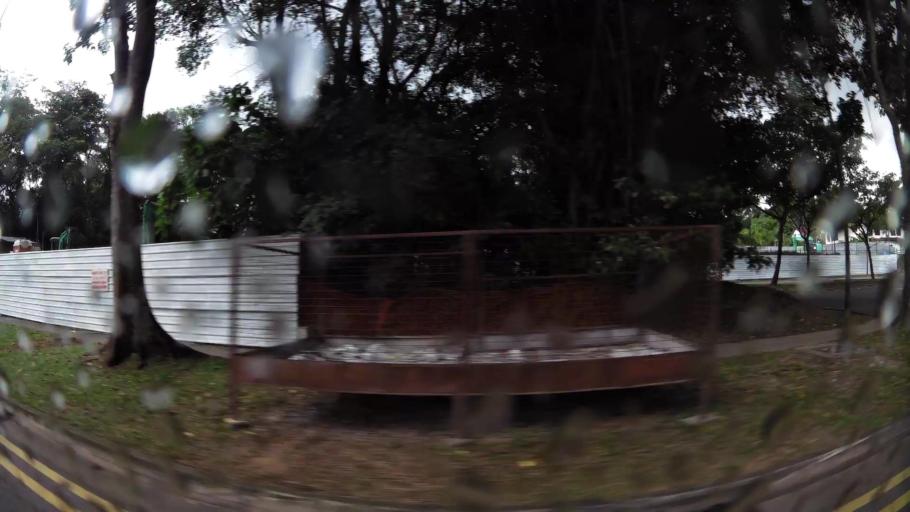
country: MY
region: Johor
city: Kampung Pasir Gudang Baru
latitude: 1.3992
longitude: 103.8726
